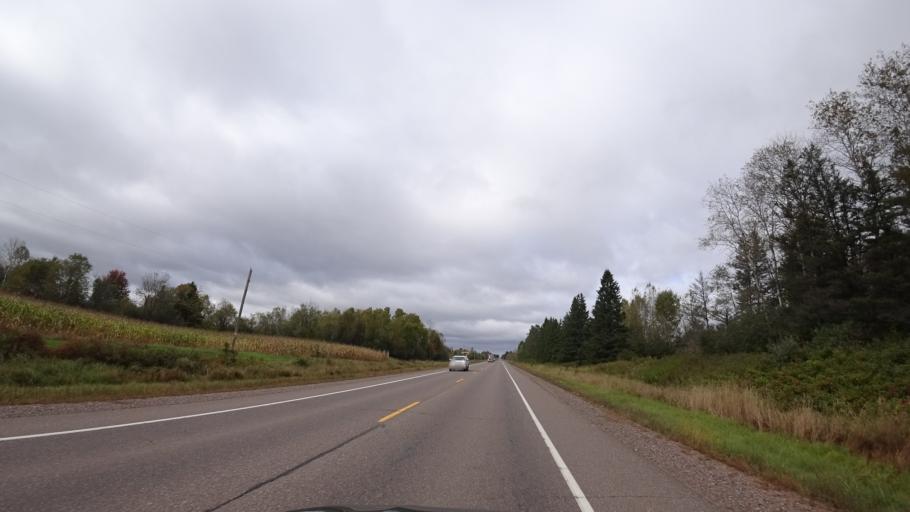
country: US
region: Wisconsin
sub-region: Rusk County
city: Ladysmith
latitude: 45.4911
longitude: -91.1115
